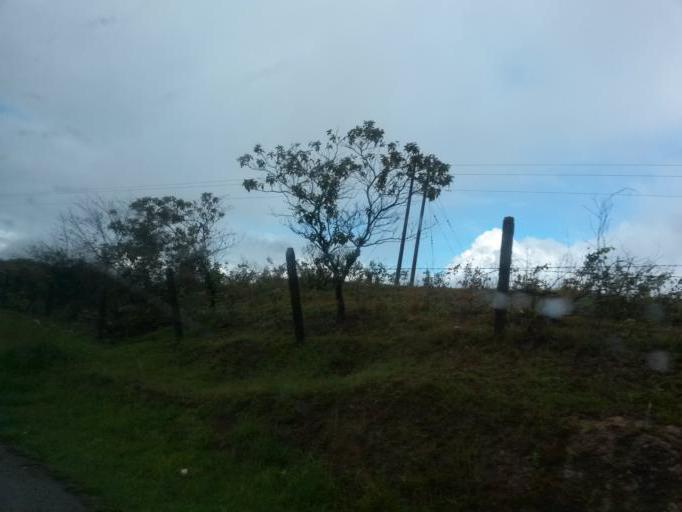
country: CO
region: Cauca
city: El Bordo
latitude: 2.1495
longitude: -76.9202
